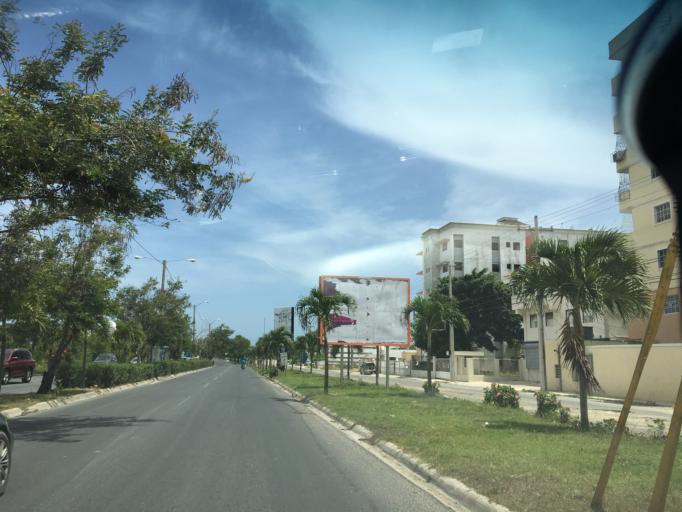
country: DO
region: La Romana
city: La Romana
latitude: 18.4262
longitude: -68.9913
